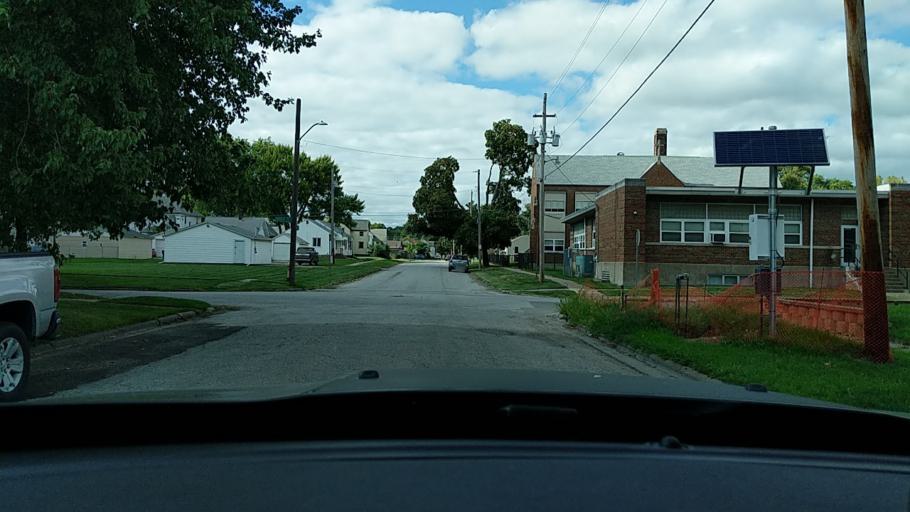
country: US
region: Illinois
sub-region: Rock Island County
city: Rock Island
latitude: 41.5133
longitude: -90.6172
